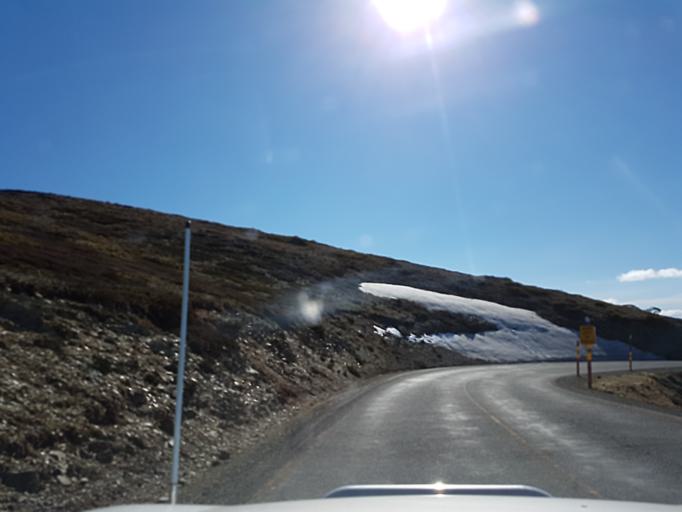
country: AU
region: Victoria
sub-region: Alpine
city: Mount Beauty
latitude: -36.9740
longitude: 147.1319
